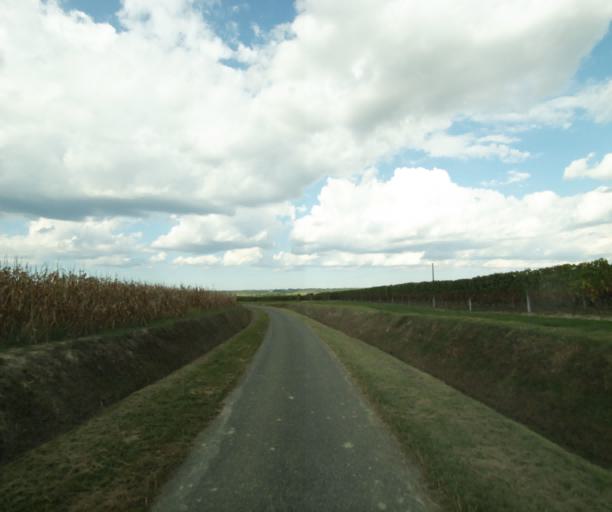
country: FR
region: Midi-Pyrenees
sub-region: Departement du Gers
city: Cazaubon
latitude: 43.8874
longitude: -0.0560
